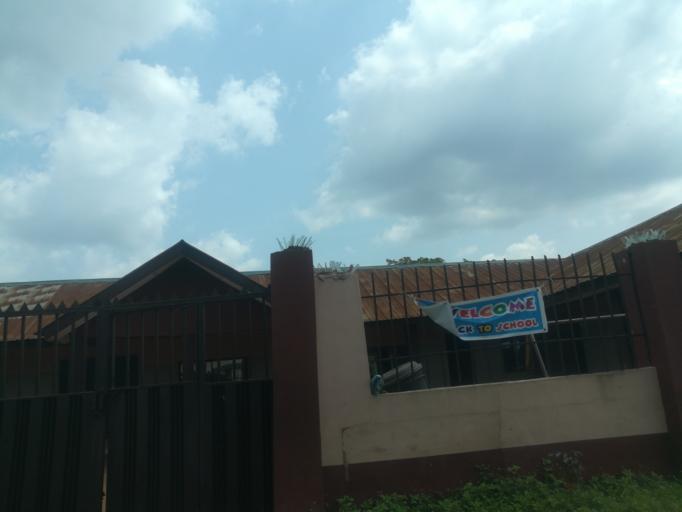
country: NG
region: Oyo
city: Ibadan
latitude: 7.4371
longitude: 3.9369
